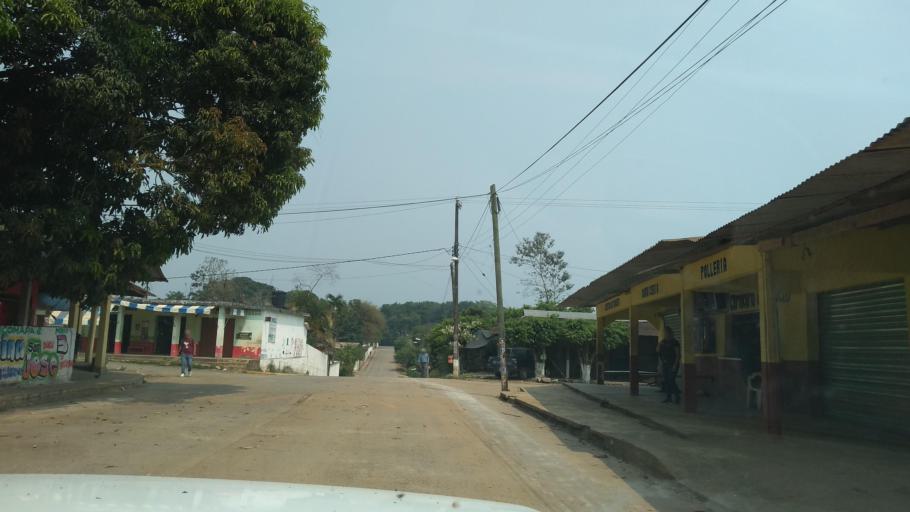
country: MX
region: Veracruz
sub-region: Tezonapa
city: Laguna Chica (Pueblo Nuevo)
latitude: 18.5439
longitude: -96.7777
